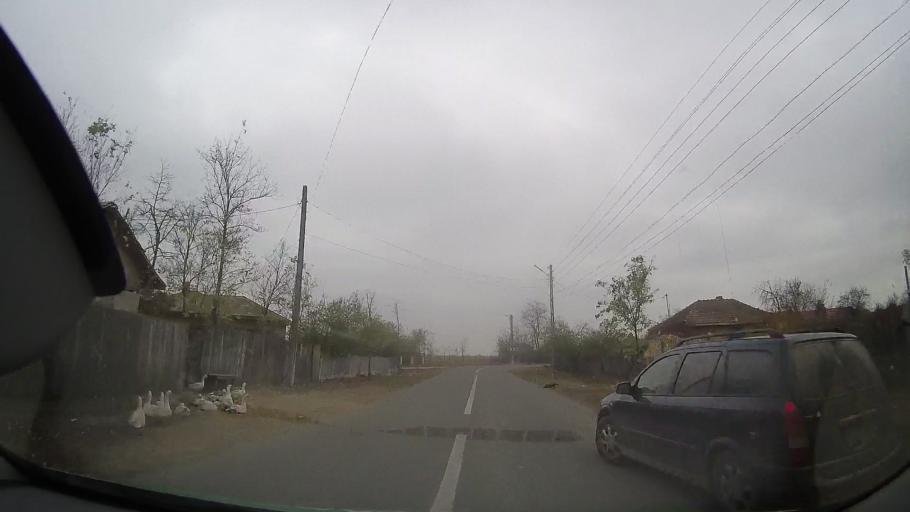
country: RO
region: Ialomita
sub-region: Comuna Grindu
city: Grindu
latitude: 44.7674
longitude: 26.9045
